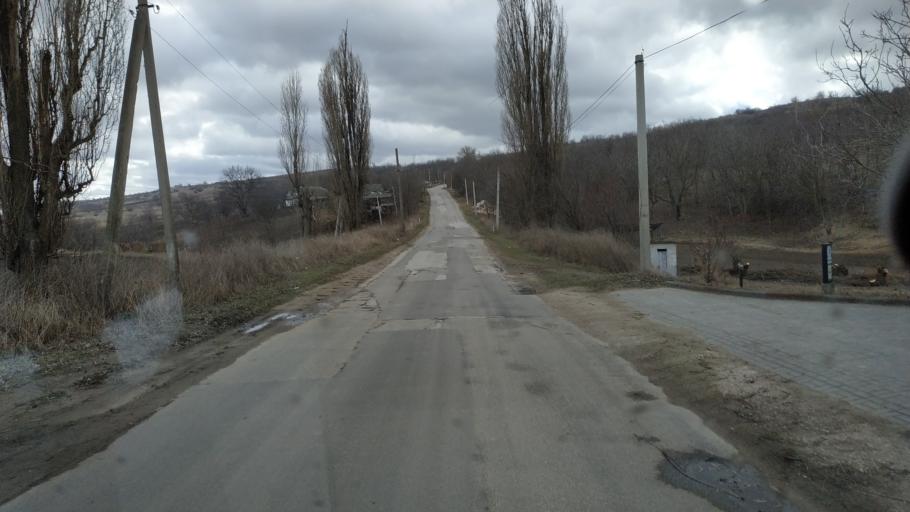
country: MD
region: Stinga Nistrului
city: Bucovat
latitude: 47.2289
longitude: 28.4263
